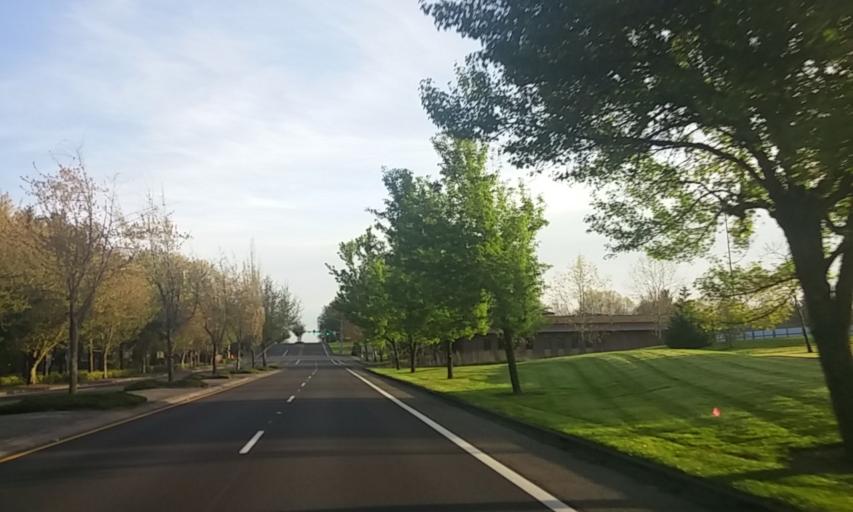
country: US
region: Oregon
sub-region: Washington County
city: Oak Hills
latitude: 45.5230
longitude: -122.8395
